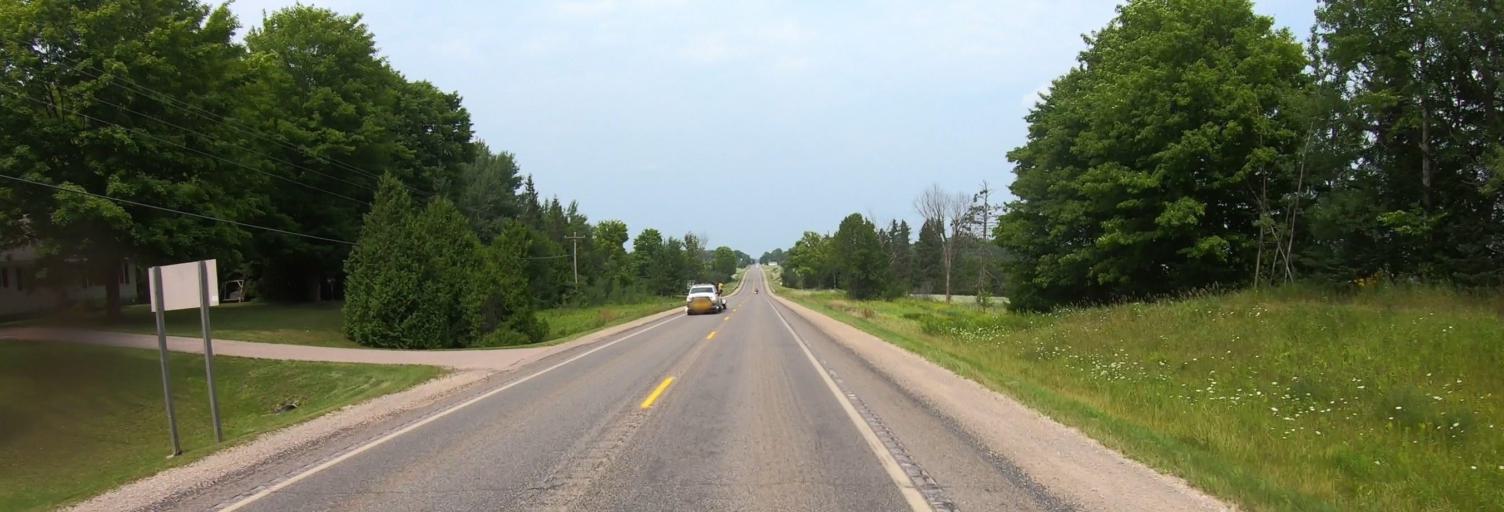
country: US
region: Michigan
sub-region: Alger County
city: Munising
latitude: 46.3348
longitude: -86.9289
